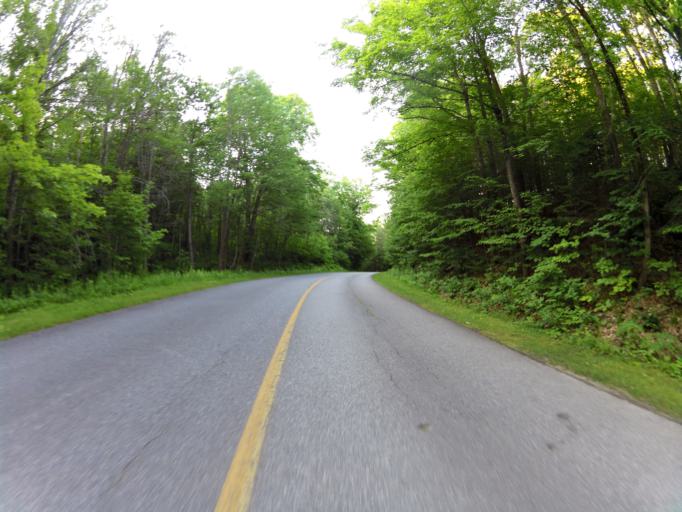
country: CA
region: Quebec
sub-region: Outaouais
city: Wakefield
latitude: 45.6092
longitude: -76.0127
